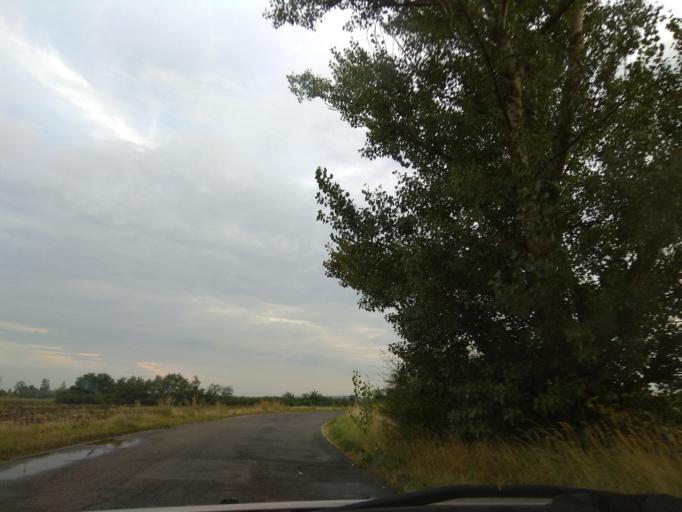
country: HU
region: Borsod-Abauj-Zemplen
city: Felsozsolca
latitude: 48.0811
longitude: 20.8453
